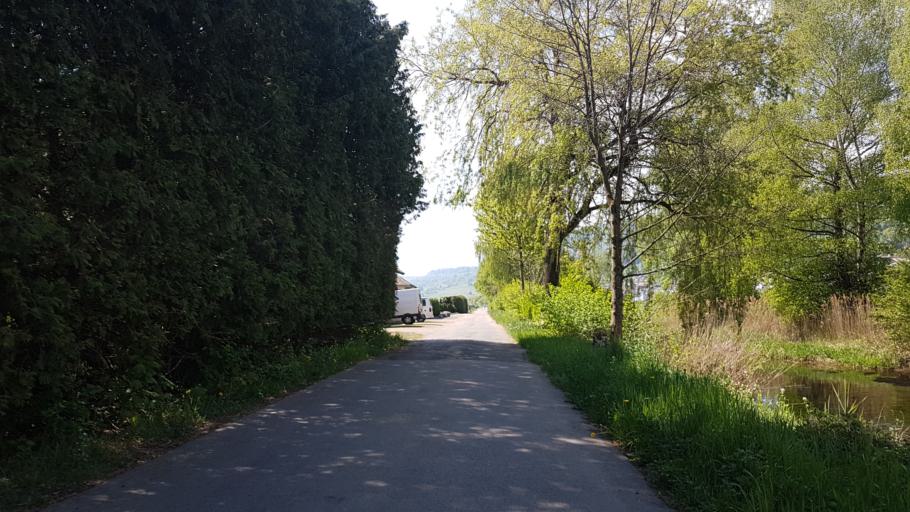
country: CH
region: Bern
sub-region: Bern-Mittelland District
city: Toffen
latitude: 46.8704
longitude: 7.4979
